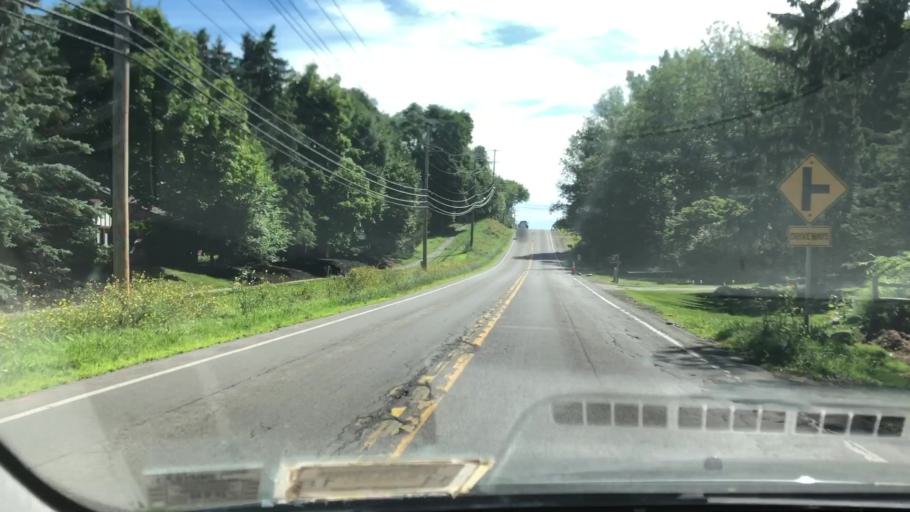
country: US
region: New York
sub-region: Monroe County
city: Fairport
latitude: 43.1084
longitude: -77.4209
